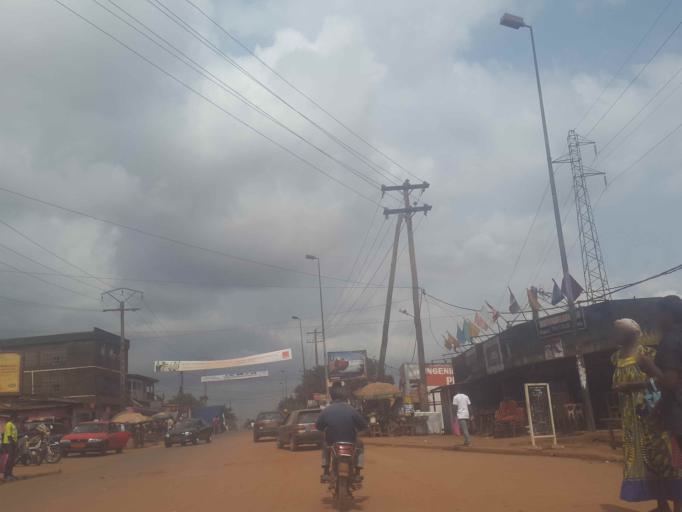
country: CM
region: Centre
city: Yaounde
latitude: 3.8754
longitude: 11.4742
